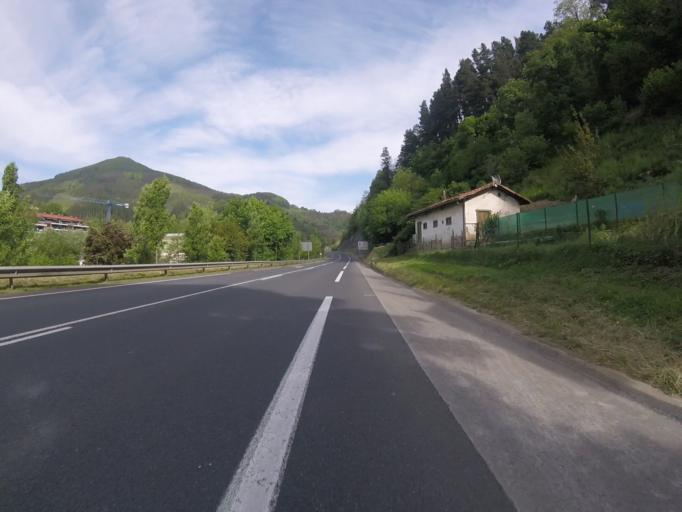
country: ES
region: Basque Country
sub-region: Provincia de Guipuzcoa
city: Urretxu
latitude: 43.0959
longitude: -2.3136
